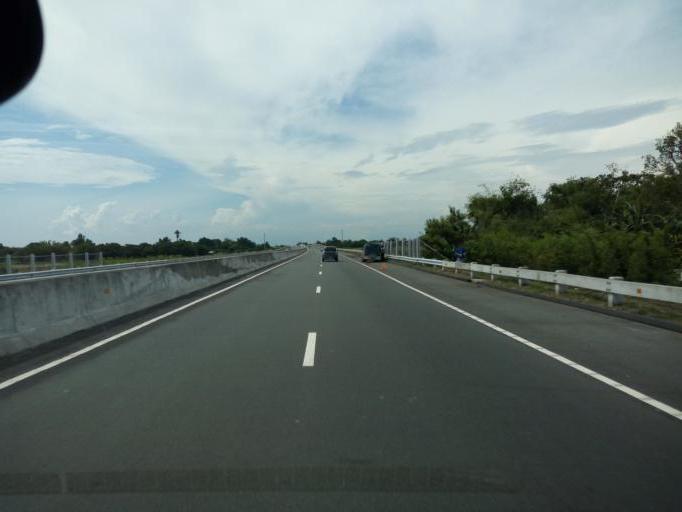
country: PH
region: Central Luzon
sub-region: Province of Nueva Ecija
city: Calancuasan Norte
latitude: 15.7880
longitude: 120.6419
